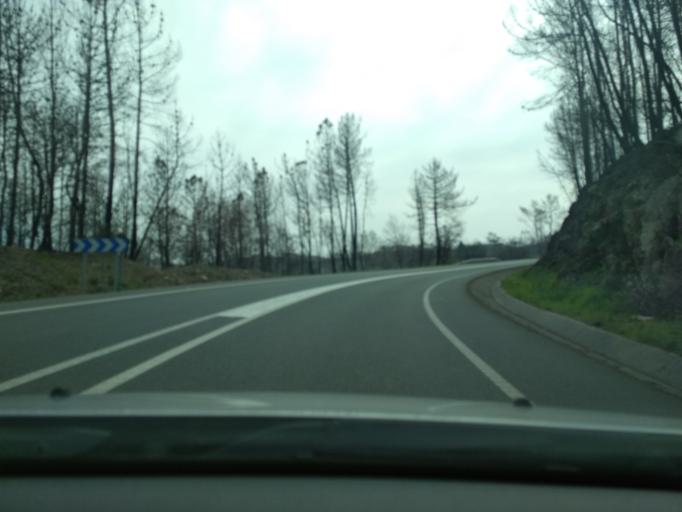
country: ES
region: Galicia
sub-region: Provincia de Pontevedra
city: Catoira
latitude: 42.6534
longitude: -8.6843
